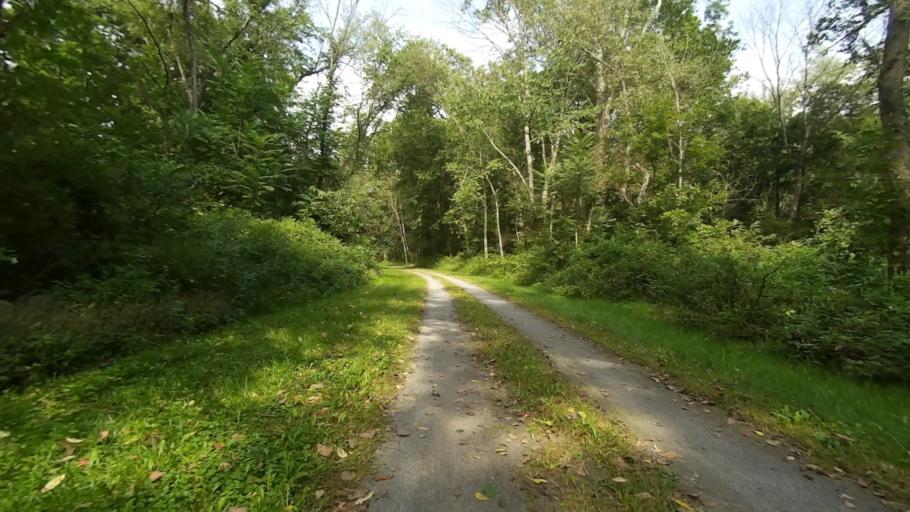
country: US
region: Pennsylvania
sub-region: Blair County
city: Williamsburg
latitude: 40.5072
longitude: -78.1642
